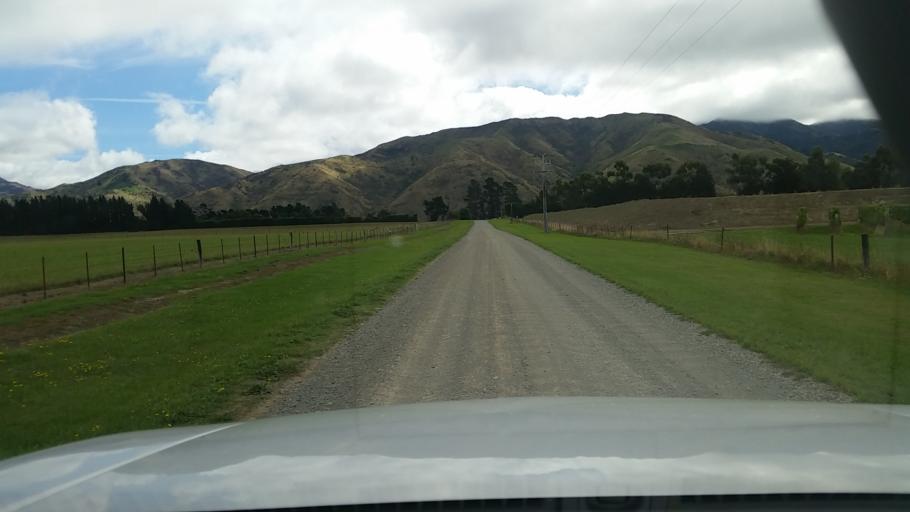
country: NZ
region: Marlborough
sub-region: Marlborough District
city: Blenheim
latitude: -41.6986
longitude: 173.9529
